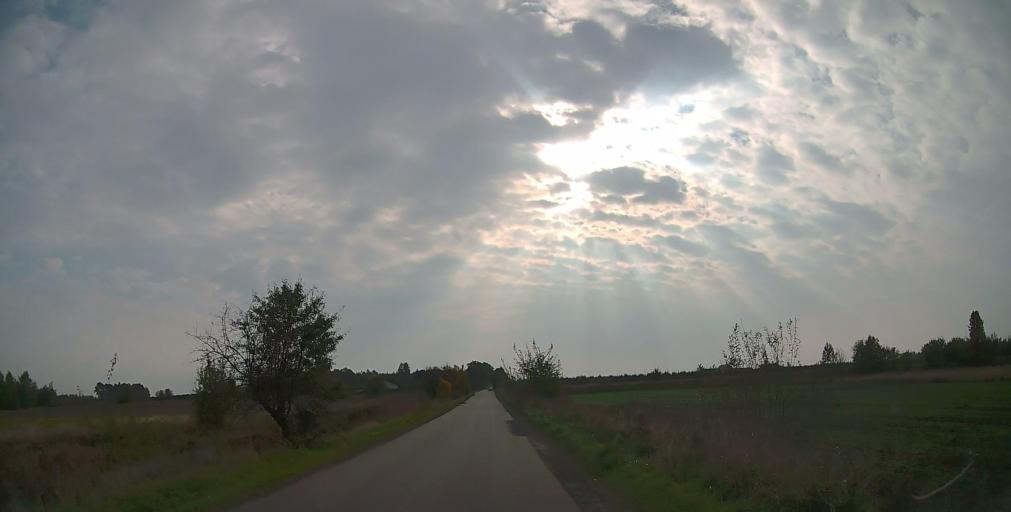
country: PL
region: Masovian Voivodeship
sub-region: Powiat grojecki
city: Mogielnica
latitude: 51.6586
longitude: 20.7145
